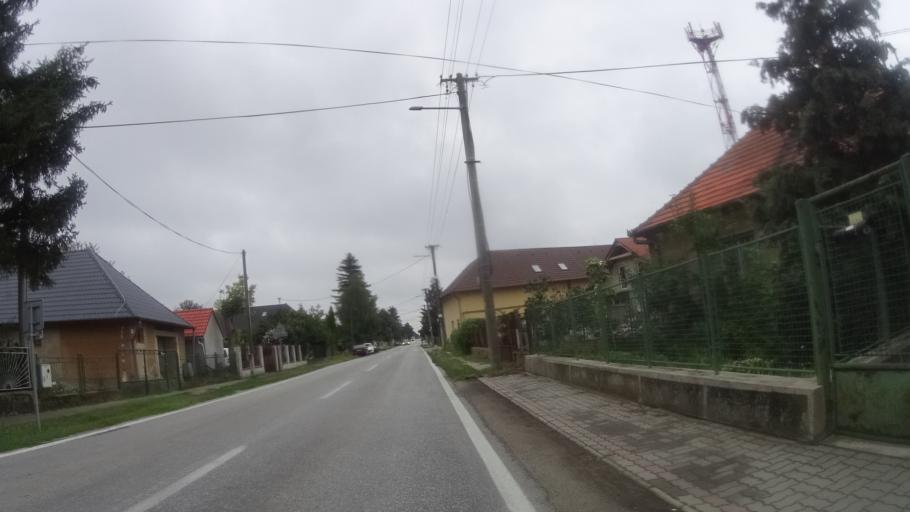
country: HU
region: Komarom-Esztergom
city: Neszmely
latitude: 47.7461
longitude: 18.3650
